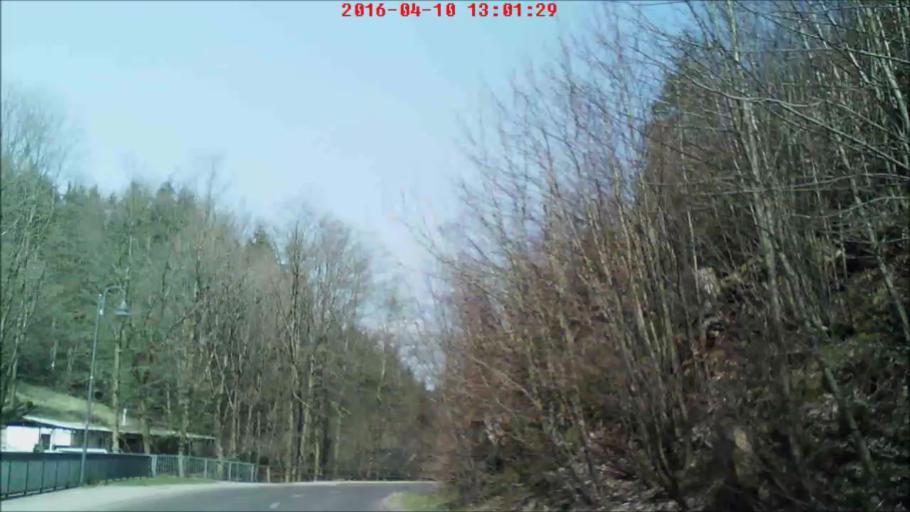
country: DE
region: Thuringia
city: Friedrichroda
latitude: 50.8459
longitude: 10.5590
